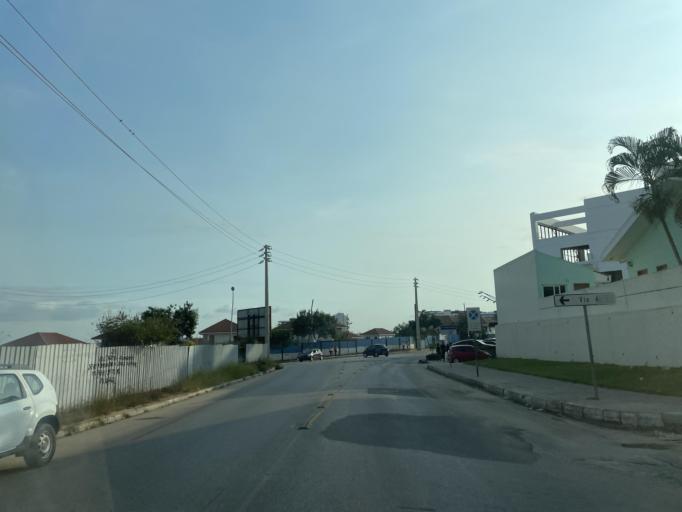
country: AO
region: Luanda
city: Luanda
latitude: -8.9222
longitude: 13.1961
